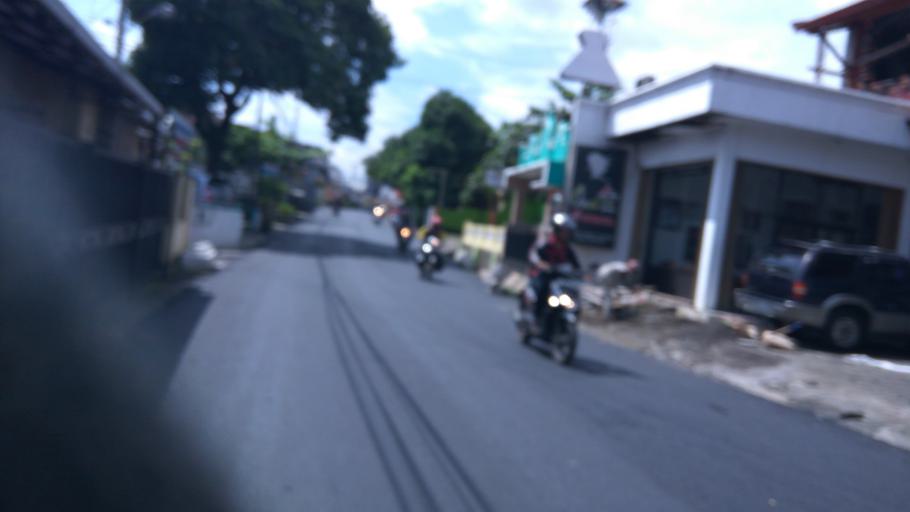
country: ID
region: Central Java
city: Ungaran
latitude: -7.1227
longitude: 110.4092
